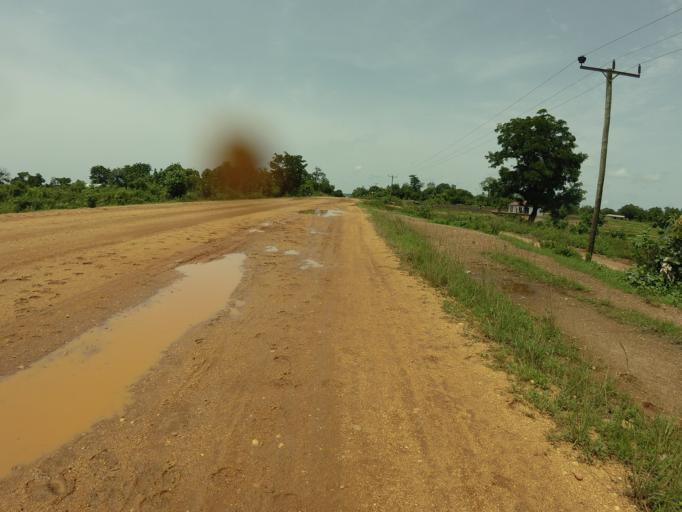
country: GH
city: Kpandae
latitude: 8.7092
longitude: 0.1530
